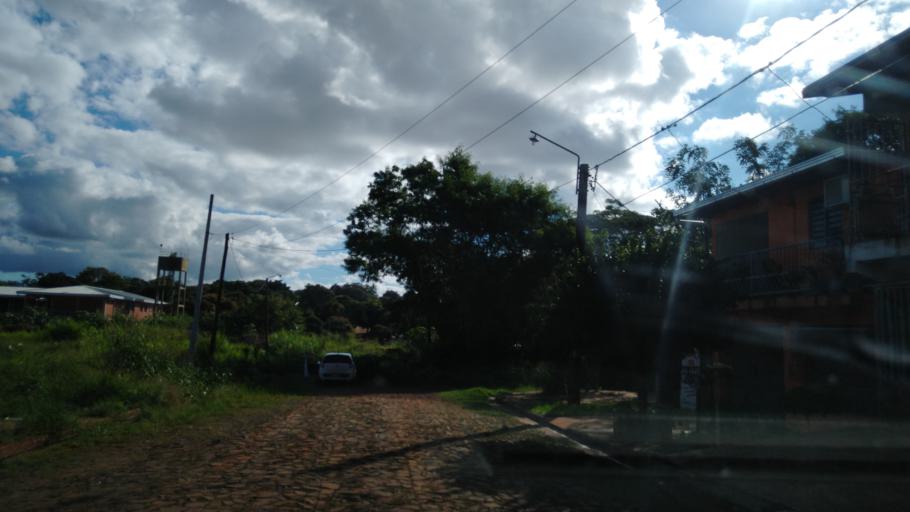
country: AR
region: Misiones
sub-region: Departamento de Capital
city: Posadas
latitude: -27.3595
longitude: -55.9252
